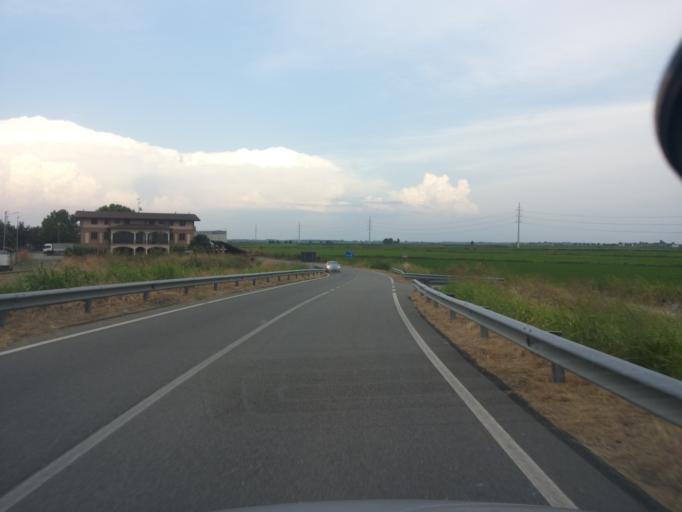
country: IT
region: Piedmont
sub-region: Provincia di Vercelli
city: Prarolo
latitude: 45.2795
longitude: 8.4747
